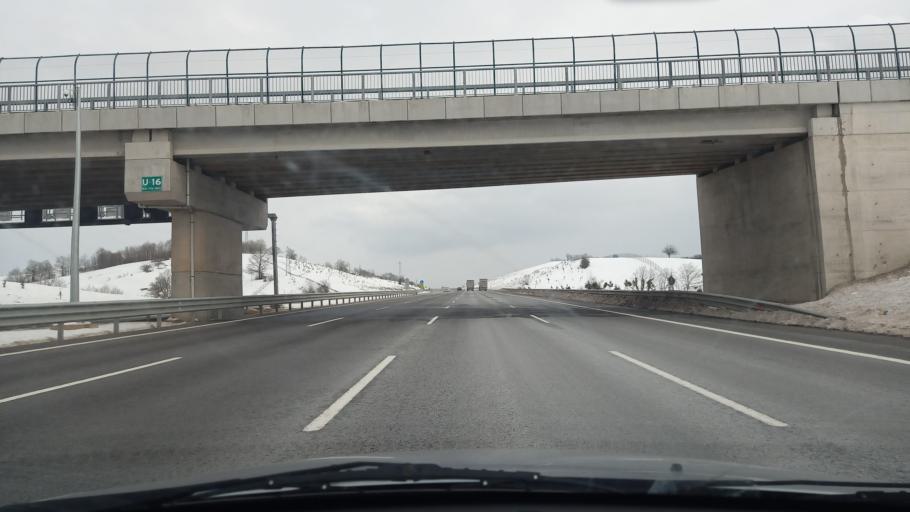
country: TR
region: Kocaeli
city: Korfez
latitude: 40.8644
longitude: 29.8131
